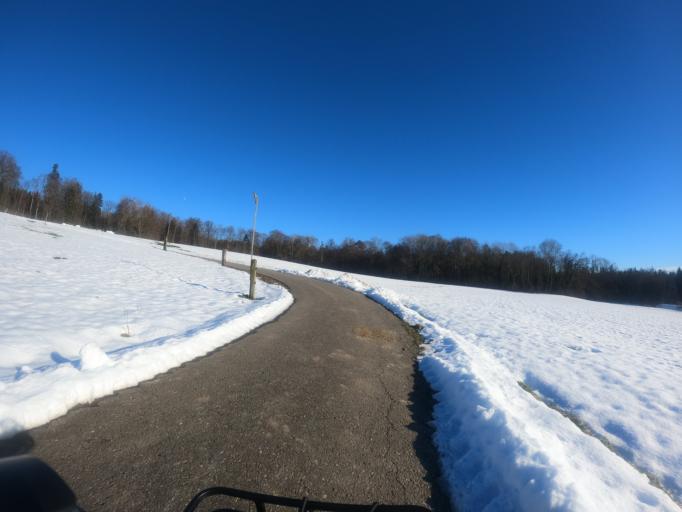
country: CH
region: Aargau
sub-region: Bezirk Bremgarten
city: Oberlunkhofen
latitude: 47.3202
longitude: 8.4028
